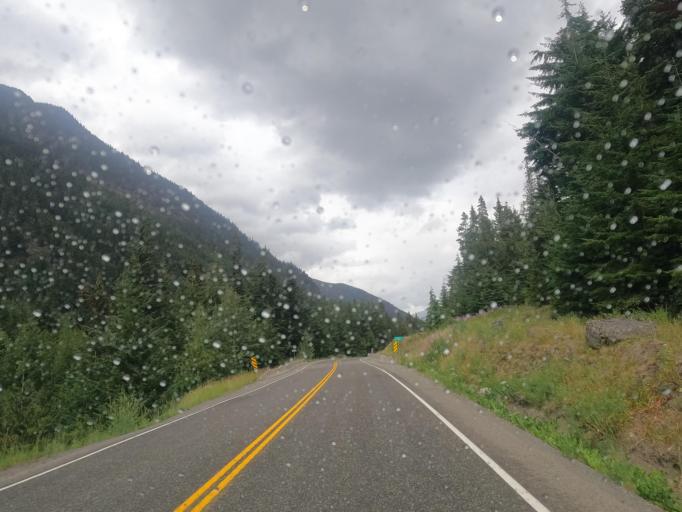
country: CA
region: British Columbia
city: Lillooet
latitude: 50.4755
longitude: -122.2250
